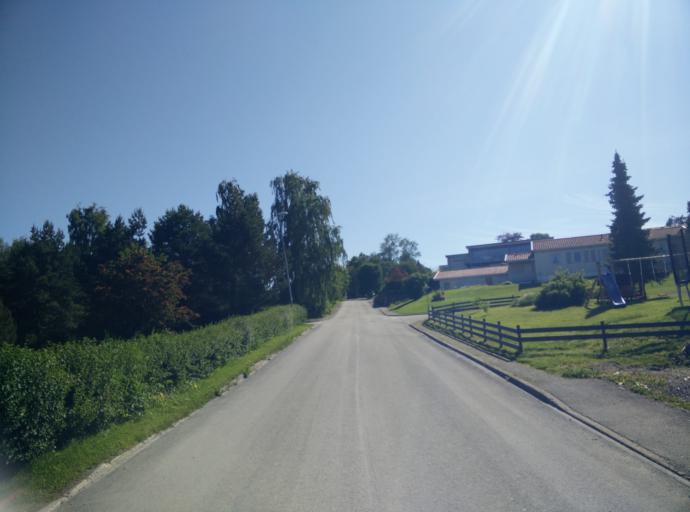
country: NO
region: Sor-Trondelag
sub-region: Trondheim
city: Trondheim
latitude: 63.4102
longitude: 10.3735
